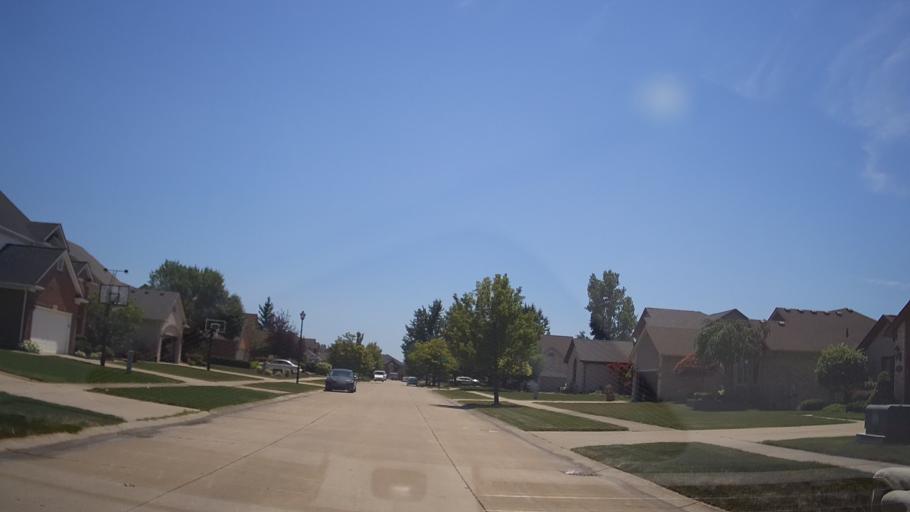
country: US
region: Michigan
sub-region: Macomb County
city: Mount Clemens
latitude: 42.6557
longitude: -82.9127
